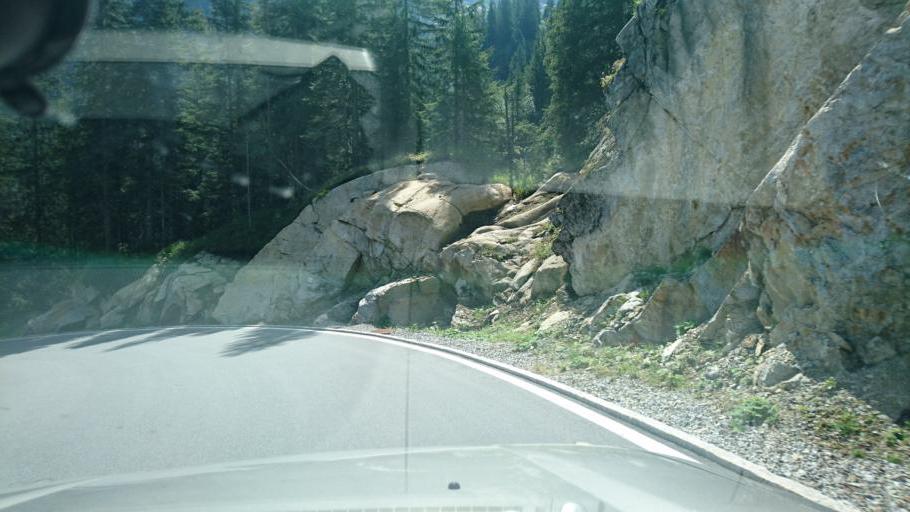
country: AT
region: Vorarlberg
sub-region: Politischer Bezirk Bludenz
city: Gaschurn
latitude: 46.9425
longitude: 10.0600
